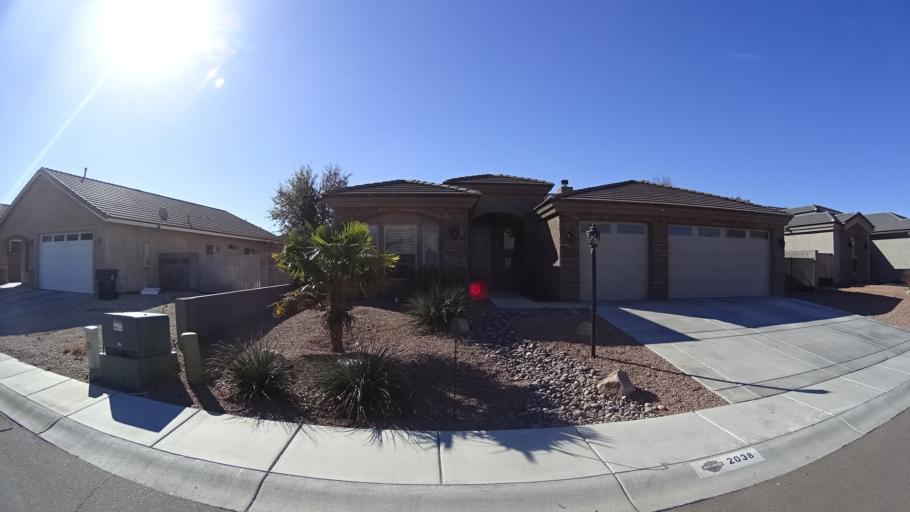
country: US
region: Arizona
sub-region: Mohave County
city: New Kingman-Butler
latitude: 35.2375
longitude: -114.0306
